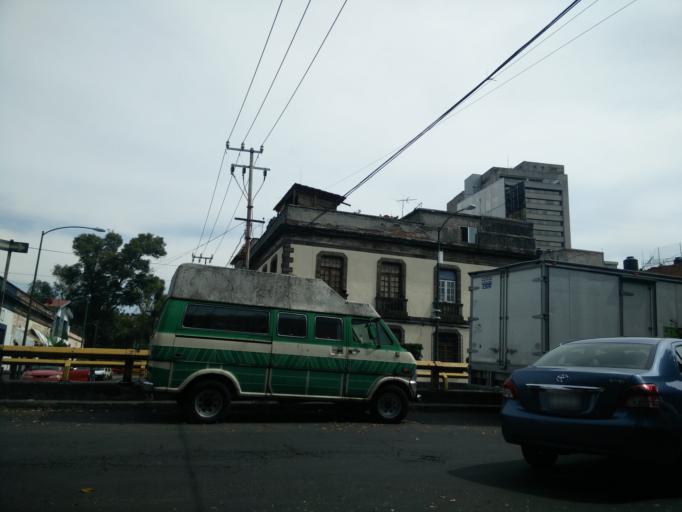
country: MX
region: Mexico City
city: Polanco
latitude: 19.4148
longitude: -99.1815
